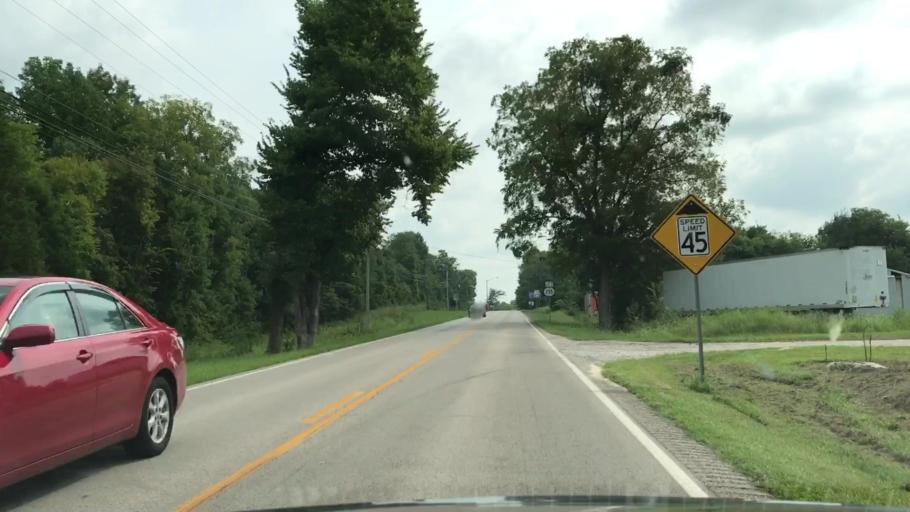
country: US
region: Kentucky
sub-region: Barren County
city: Cave City
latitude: 37.0920
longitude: -86.0580
